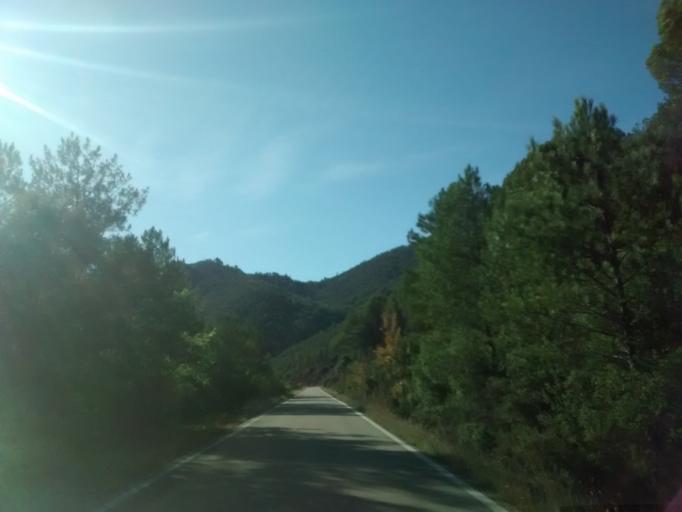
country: ES
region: Aragon
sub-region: Provincia de Huesca
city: Loarre
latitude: 42.3893
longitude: -0.6692
